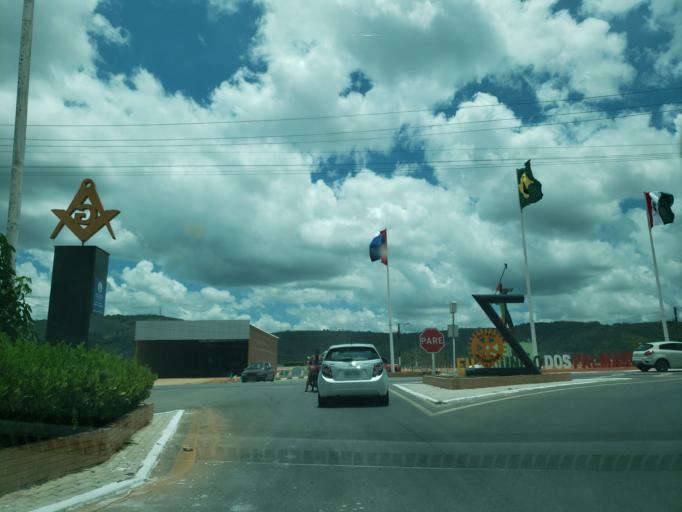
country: BR
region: Alagoas
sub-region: Uniao Dos Palmares
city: Uniao dos Palmares
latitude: -9.1664
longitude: -36.0214
